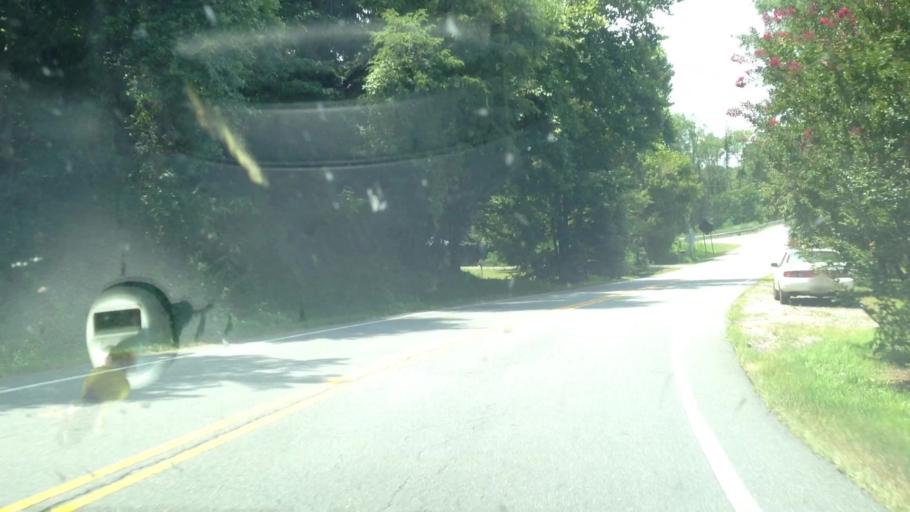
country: US
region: North Carolina
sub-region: Stokes County
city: Walnut Cove
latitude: 36.3181
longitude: -80.0471
